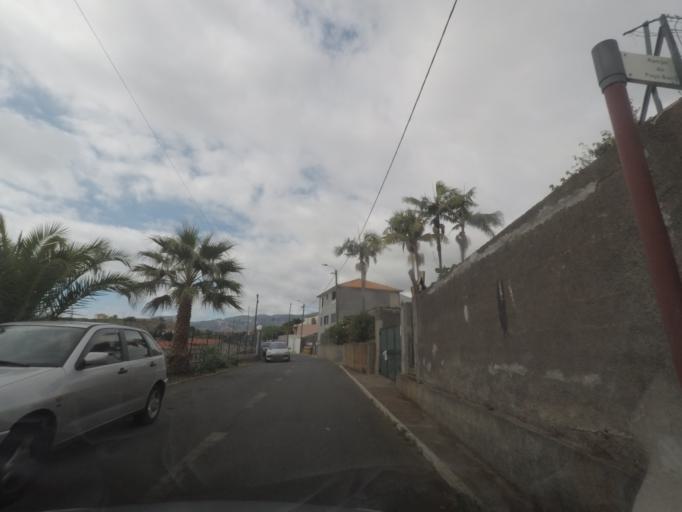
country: PT
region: Madeira
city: Camara de Lobos
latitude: 32.6538
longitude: -16.9443
